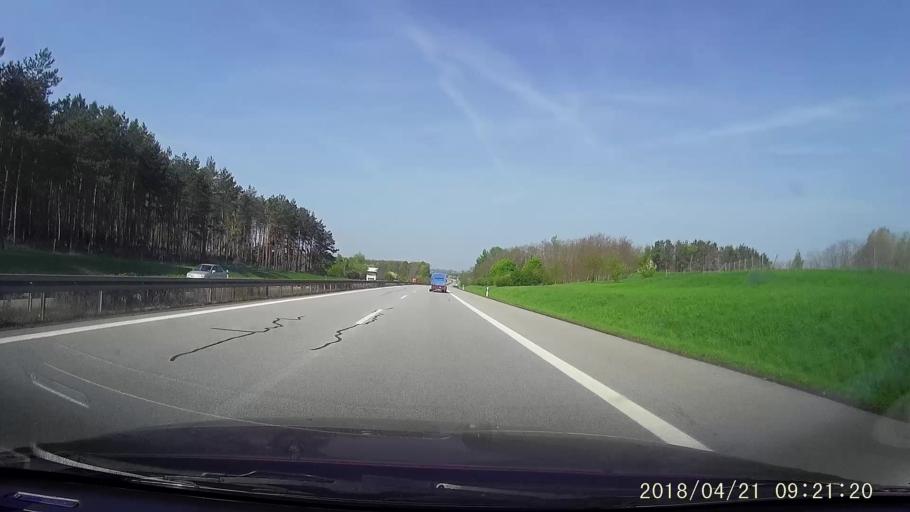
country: DE
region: Saxony
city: Guttau
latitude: 51.2091
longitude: 14.5842
